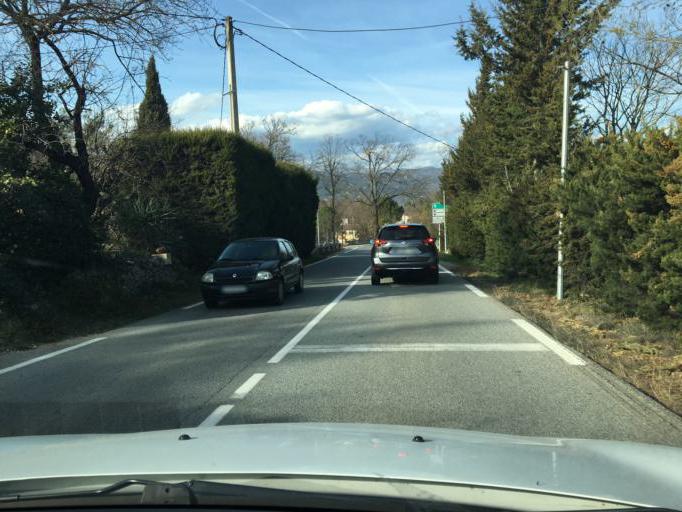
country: FR
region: Provence-Alpes-Cote d'Azur
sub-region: Departement du Var
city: Saint-Paul-en-Foret
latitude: 43.5951
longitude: 6.6893
